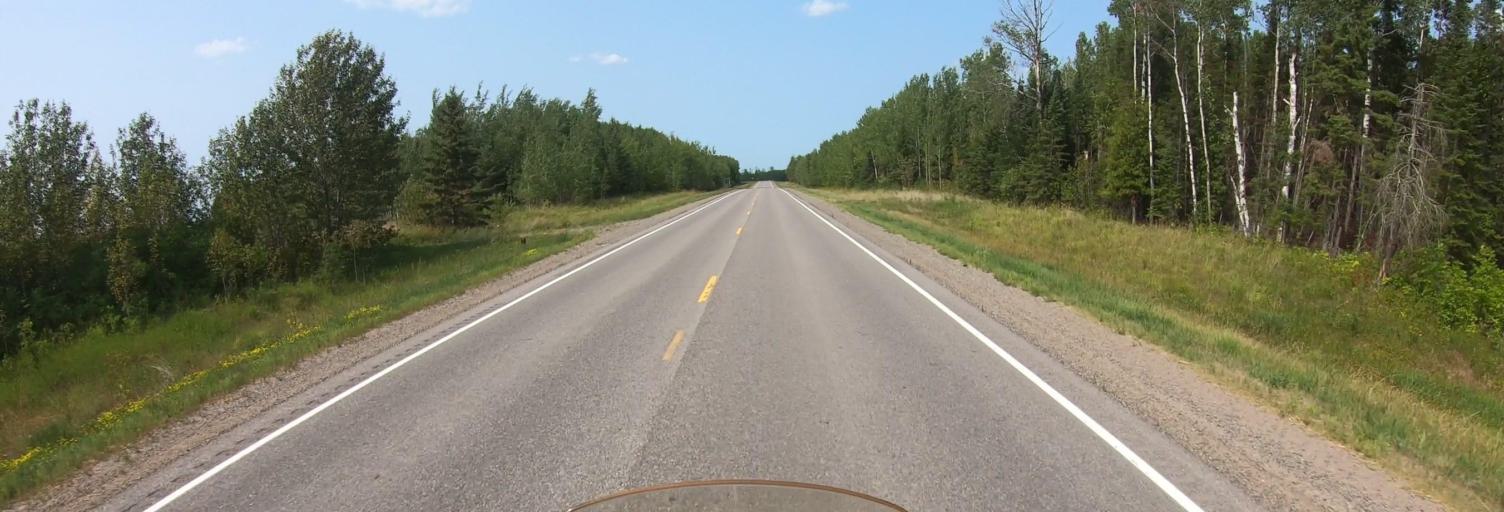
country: US
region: Minnesota
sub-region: Lake of the Woods County
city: Baudette
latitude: 48.6379
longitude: -94.1288
